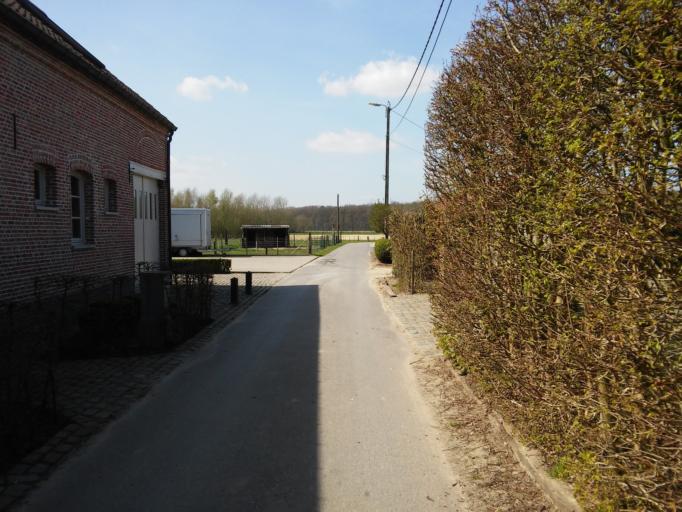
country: BE
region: Flanders
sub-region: Provincie Vlaams-Brabant
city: Kampenhout
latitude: 50.9637
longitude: 4.5511
